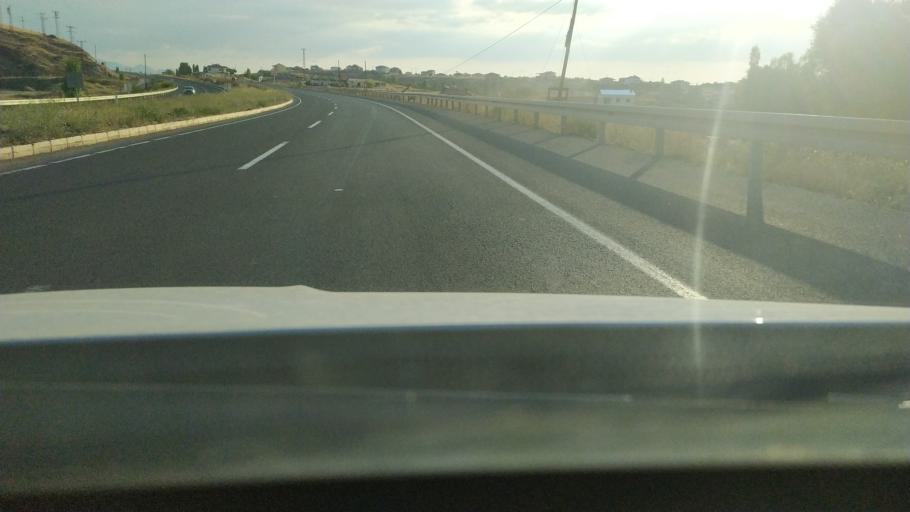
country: TR
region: Kayseri
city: Muncusun
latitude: 38.8734
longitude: 35.7021
